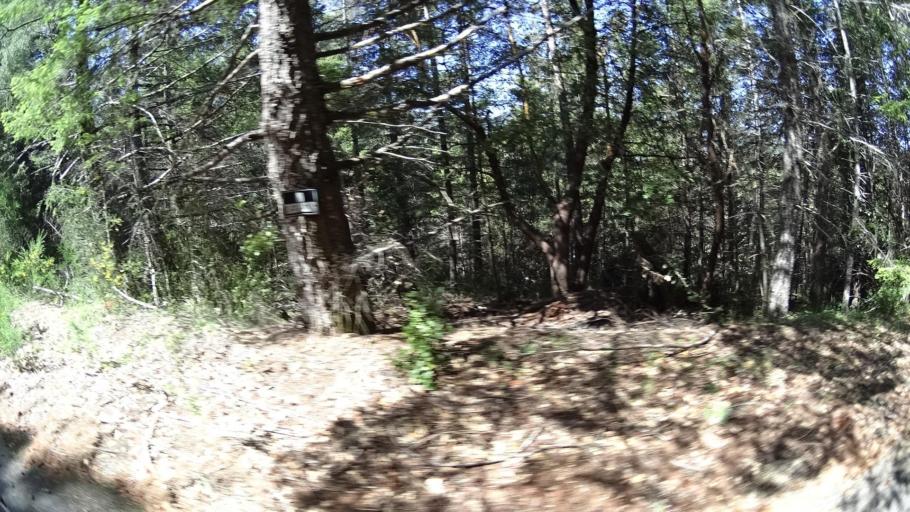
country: US
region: California
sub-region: Humboldt County
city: Redway
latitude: 40.1921
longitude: -124.0943
